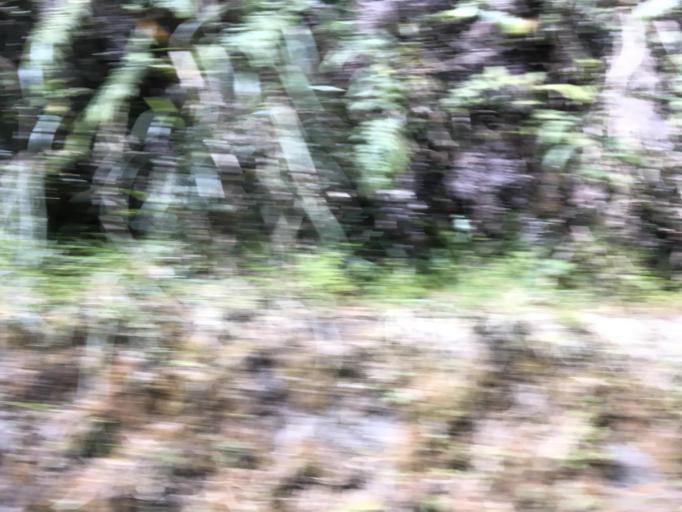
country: TW
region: Taiwan
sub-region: Yilan
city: Yilan
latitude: 24.5172
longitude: 121.5226
